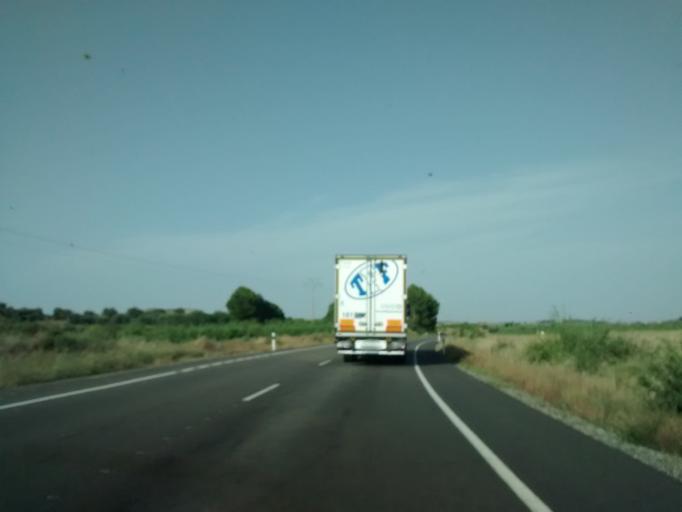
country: ES
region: Aragon
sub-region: Provincia de Zaragoza
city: Bulbuente
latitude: 41.8275
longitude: -1.5815
